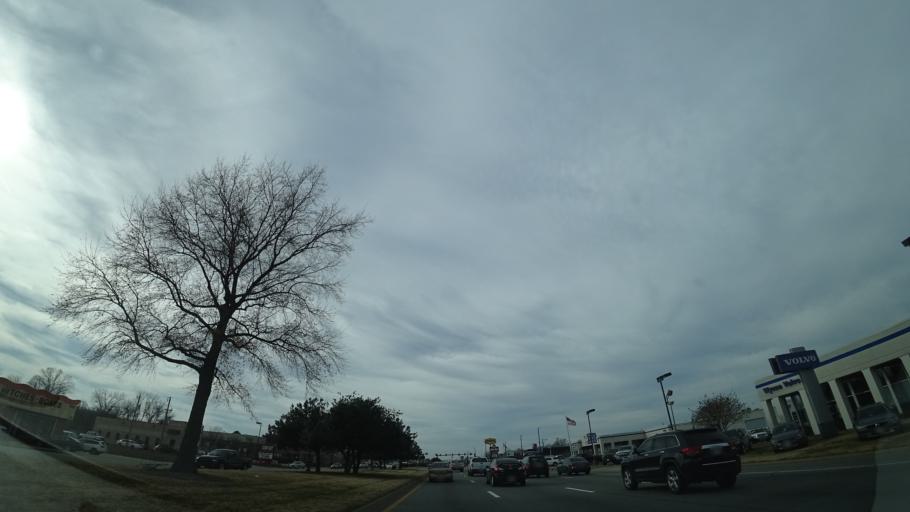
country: US
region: Virginia
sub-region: City of Hampton
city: Hampton
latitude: 37.0438
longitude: -76.3788
